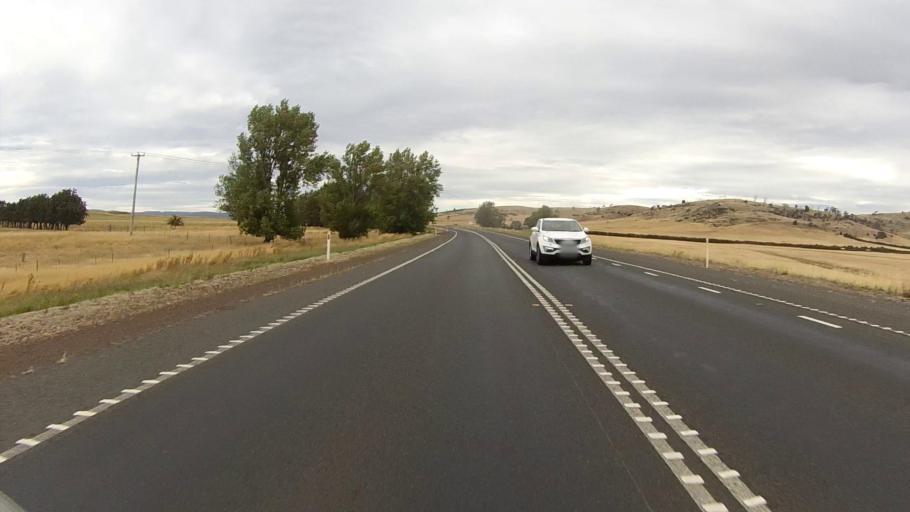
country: AU
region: Tasmania
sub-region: Brighton
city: Bridgewater
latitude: -42.3685
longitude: 147.3342
